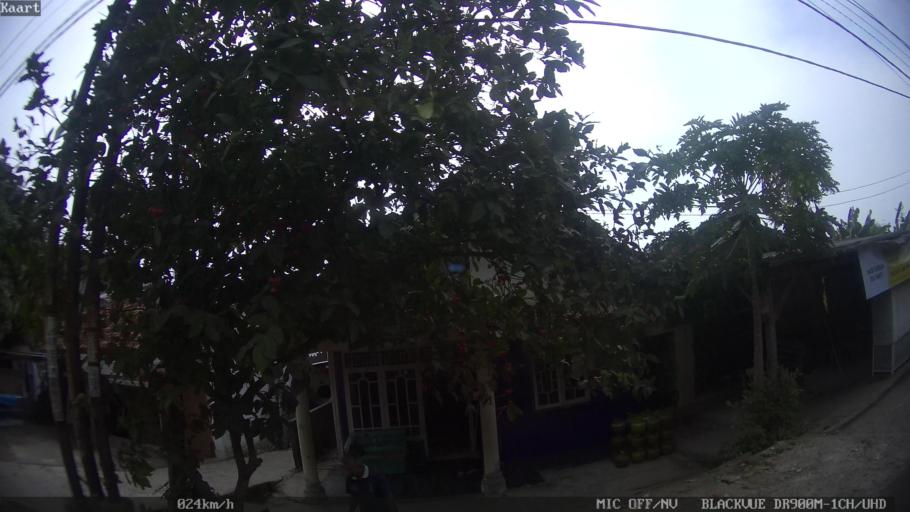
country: ID
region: Lampung
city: Bandarlampung
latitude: -5.4233
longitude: 105.2801
